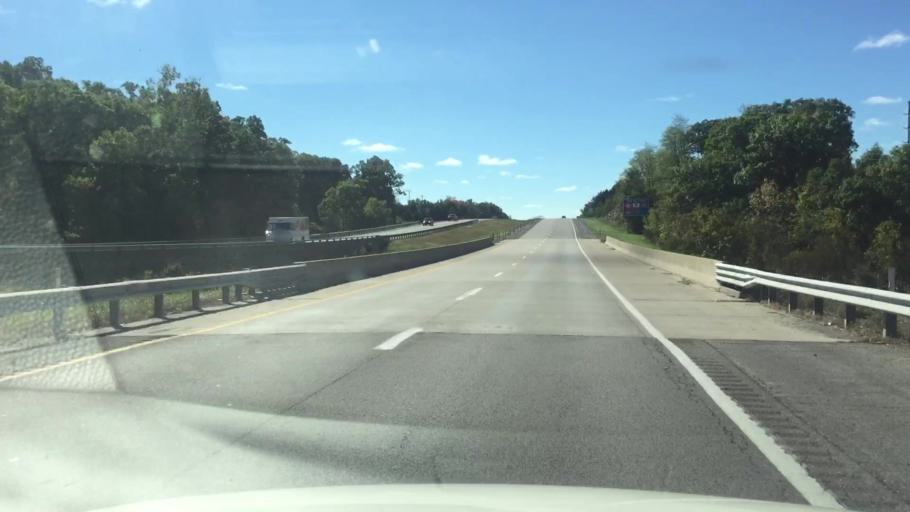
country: US
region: Missouri
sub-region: Boone County
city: Columbia
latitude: 38.9273
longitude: -92.2948
